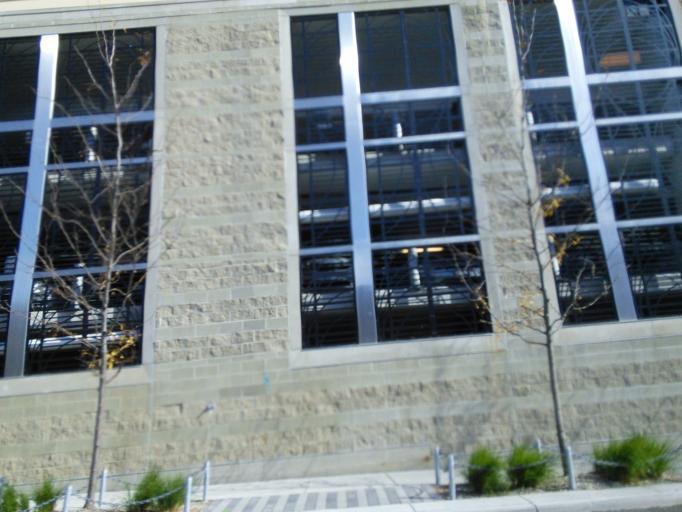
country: US
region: Michigan
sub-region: Washtenaw County
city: Ann Arbor
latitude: 42.2803
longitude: -83.7510
